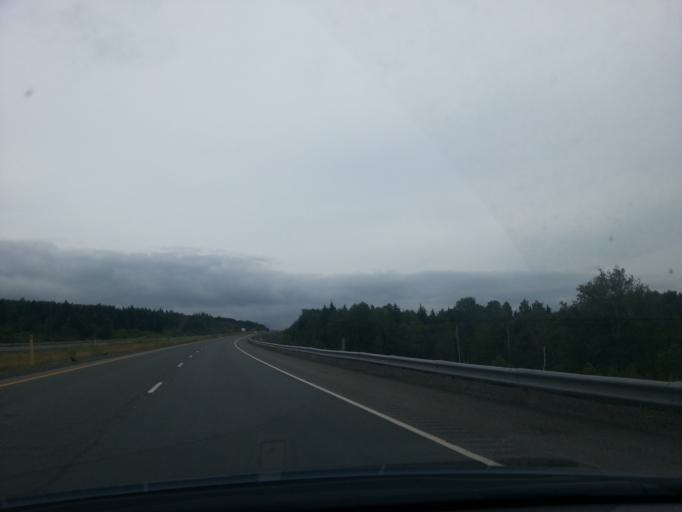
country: CA
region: New Brunswick
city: Harrison Brook
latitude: 47.2858
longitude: -68.0327
